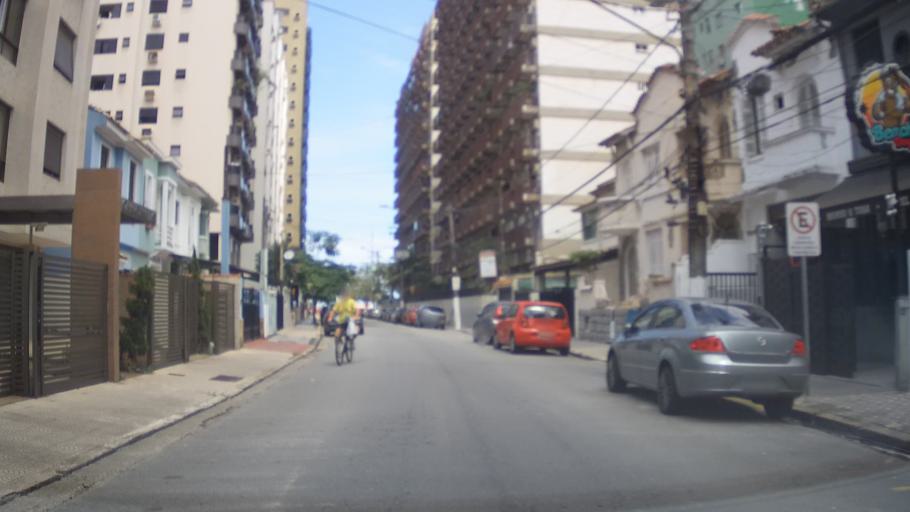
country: BR
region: Sao Paulo
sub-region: Santos
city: Santos
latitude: -23.9664
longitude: -46.3445
